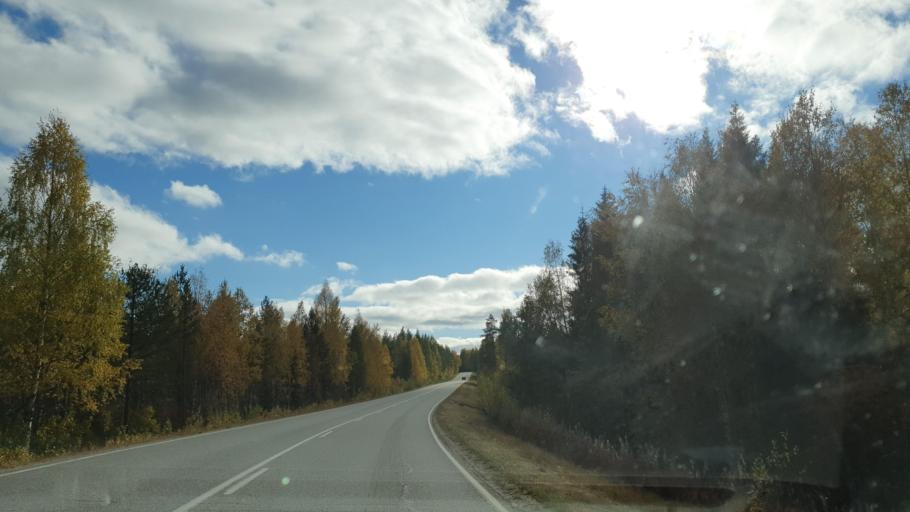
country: FI
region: Kainuu
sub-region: Kehys-Kainuu
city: Puolanka
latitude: 65.1457
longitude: 27.6792
